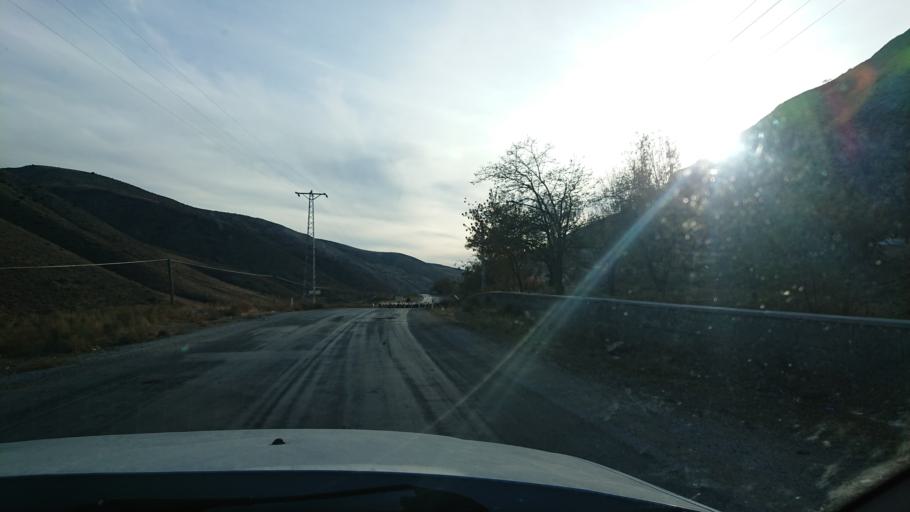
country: TR
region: Ankara
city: Sereflikochisar
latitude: 38.7608
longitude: 33.6971
